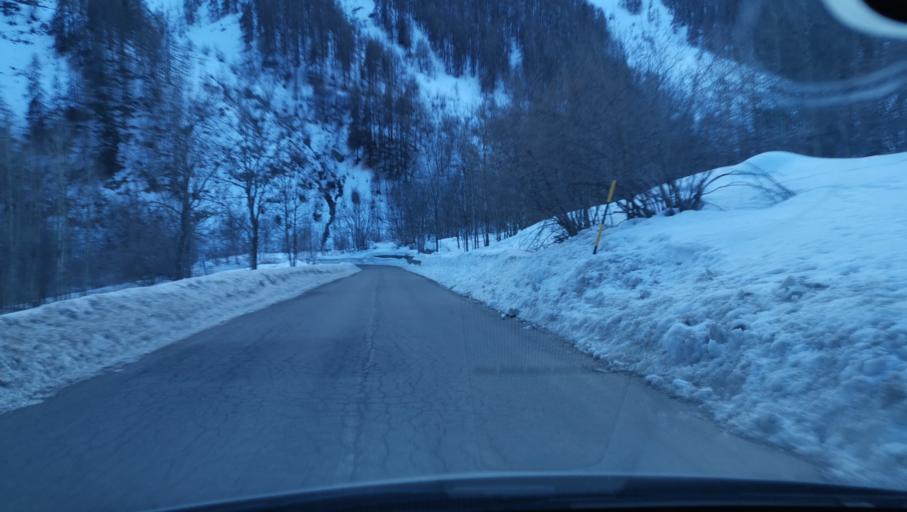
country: IT
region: Piedmont
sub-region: Provincia di Cuneo
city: Bersezio
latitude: 44.3595
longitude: 6.9988
